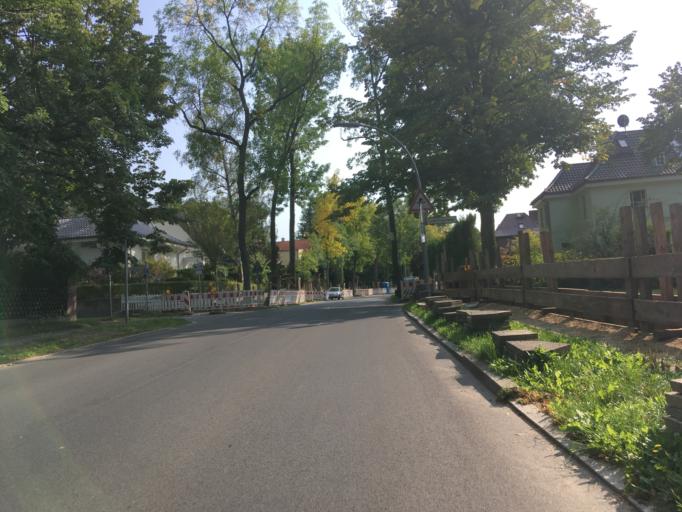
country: DE
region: Berlin
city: Frohnau
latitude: 52.6331
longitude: 13.2810
